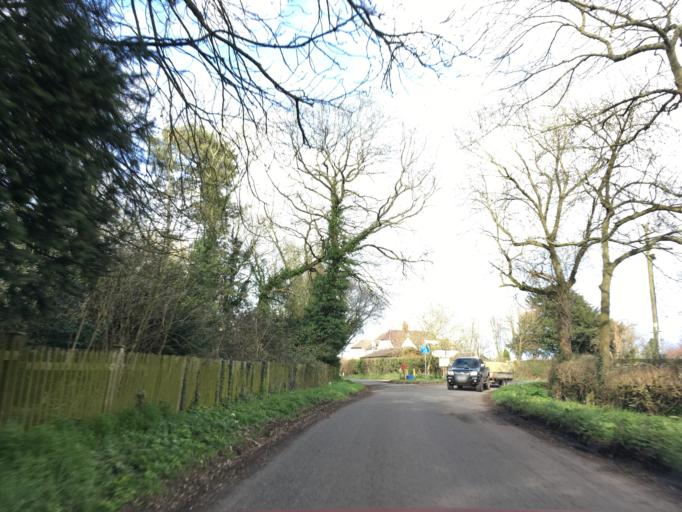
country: GB
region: England
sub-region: Gloucestershire
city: Mitcheldean
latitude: 51.8282
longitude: -2.4046
